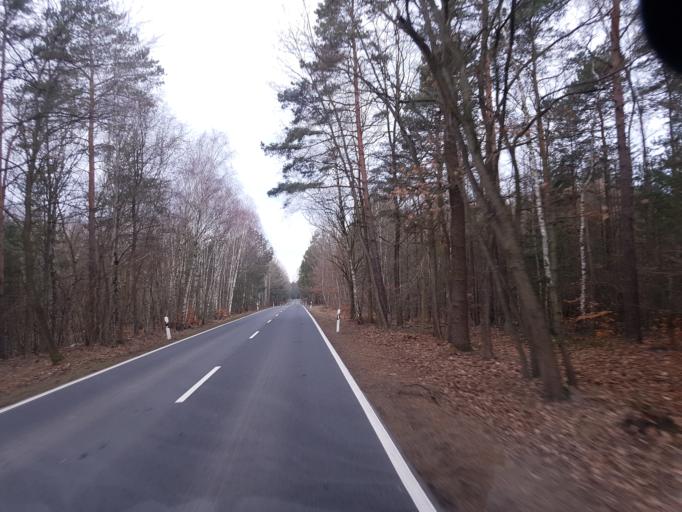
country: DE
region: Brandenburg
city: Sallgast
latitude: 51.5812
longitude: 13.8385
